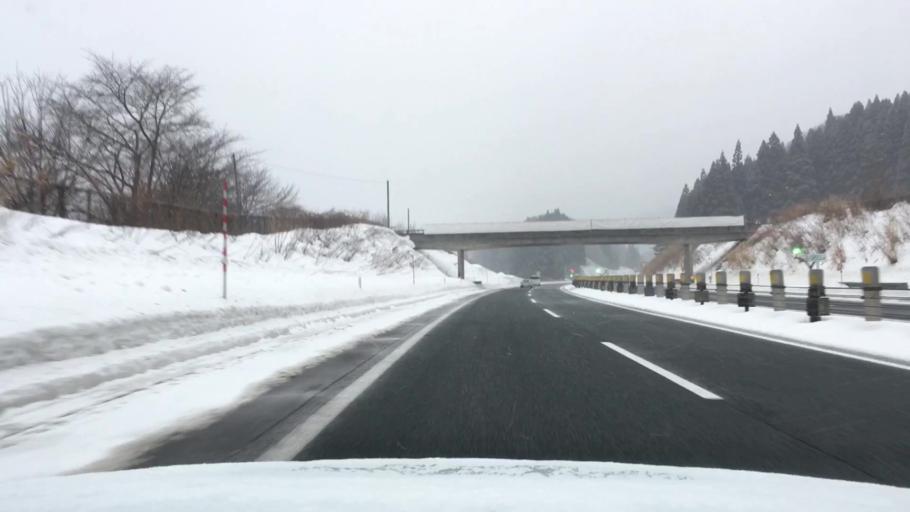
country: JP
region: Akita
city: Hanawa
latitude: 40.1099
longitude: 141.0392
